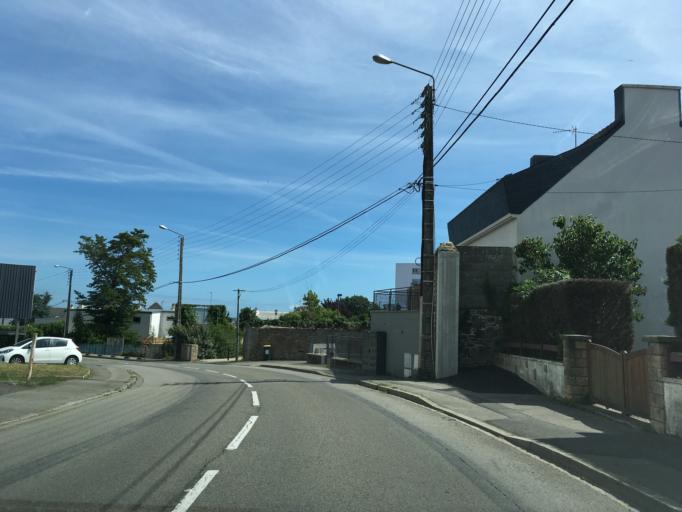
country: FR
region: Brittany
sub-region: Departement du Morbihan
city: Lorient
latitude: 47.7501
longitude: -3.3837
